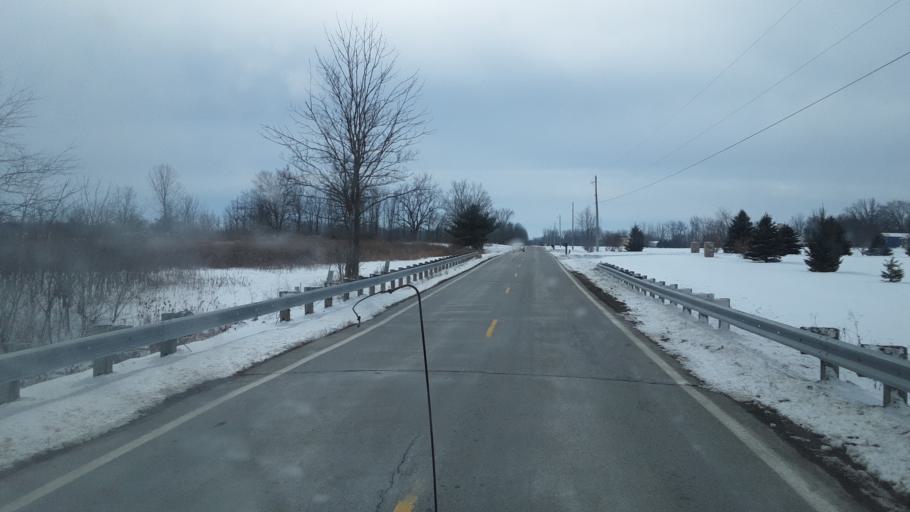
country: US
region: Ohio
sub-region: Madison County
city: Choctaw Lake
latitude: 39.9656
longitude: -83.5030
